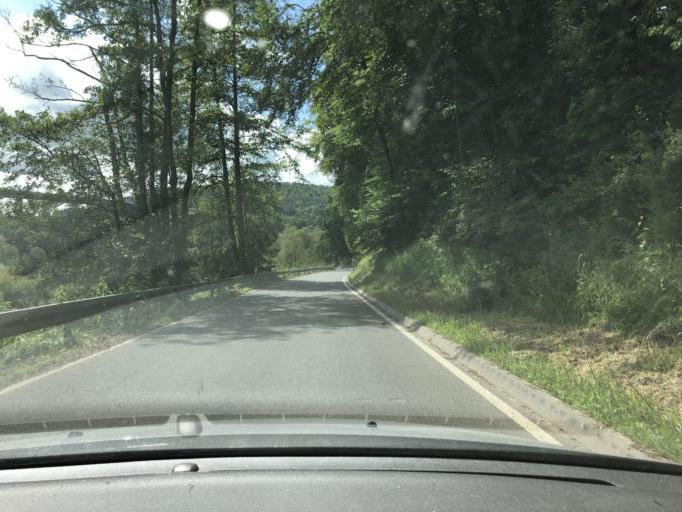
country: DE
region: Hesse
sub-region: Regierungsbezirk Kassel
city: Malsfeld
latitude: 51.0685
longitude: 9.5754
